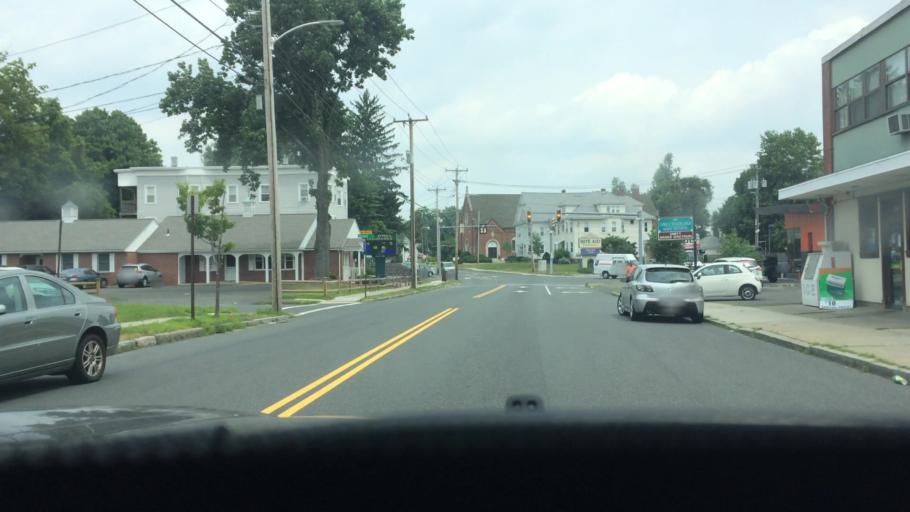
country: US
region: Massachusetts
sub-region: Hampden County
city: Chicopee
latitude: 42.1468
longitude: -72.5798
